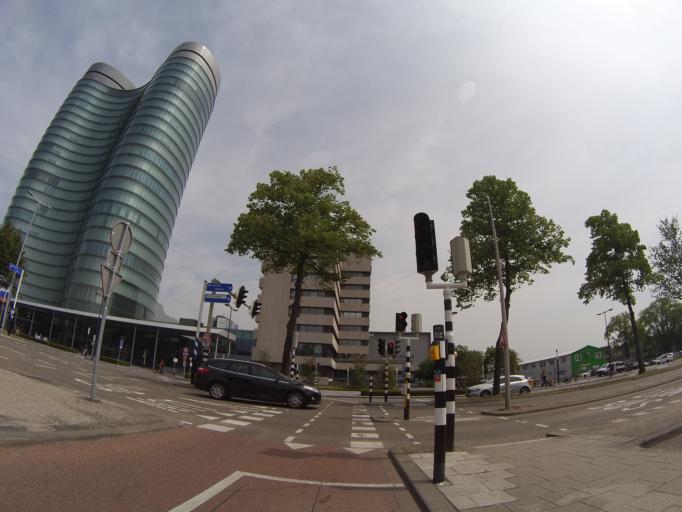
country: NL
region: Utrecht
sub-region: Gemeente Utrecht
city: Utrecht
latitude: 52.0848
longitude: 5.1088
